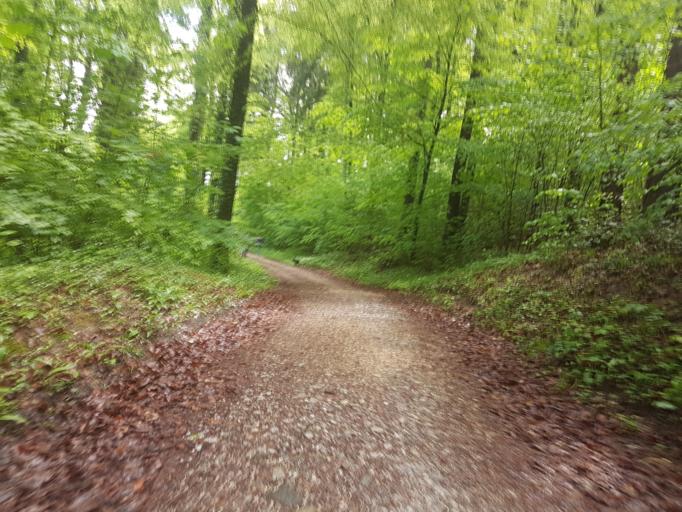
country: CH
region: Vaud
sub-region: Ouest Lausannois District
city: Bussigny
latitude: 46.5557
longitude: 6.5285
